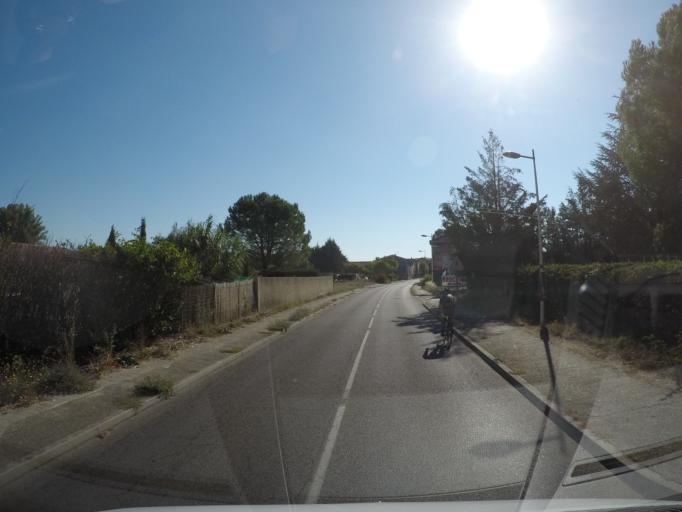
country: FR
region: Languedoc-Roussillon
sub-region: Departement du Gard
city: Boisset-et-Gaujac
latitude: 44.0275
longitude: 4.0200
